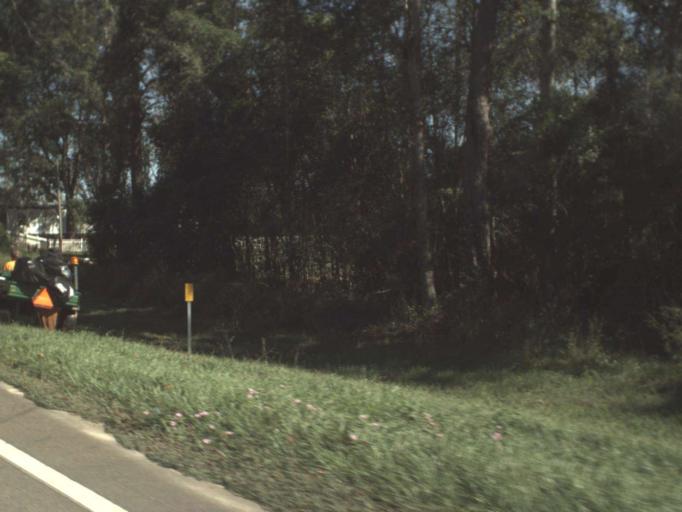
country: US
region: Florida
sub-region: Walton County
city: DeFuniak Springs
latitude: 30.6737
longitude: -85.9365
